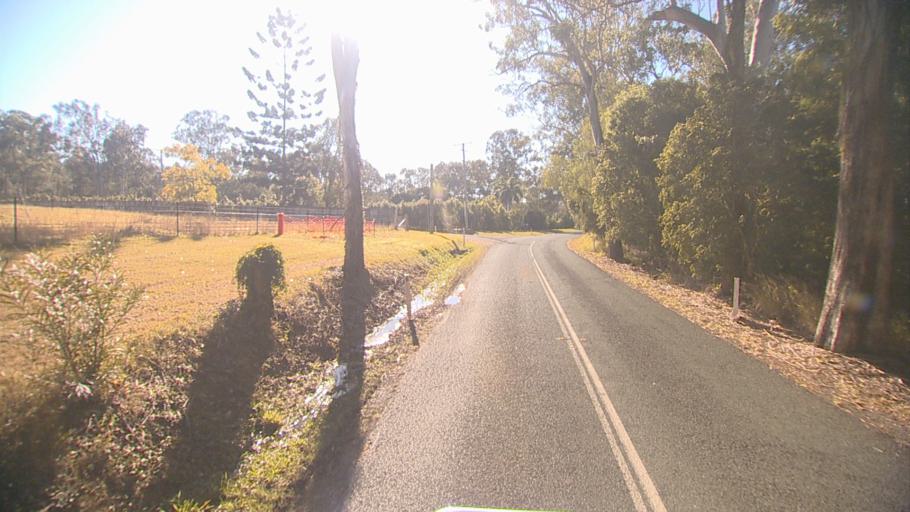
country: AU
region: Queensland
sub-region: Logan
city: Windaroo
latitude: -27.7969
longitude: 153.1741
